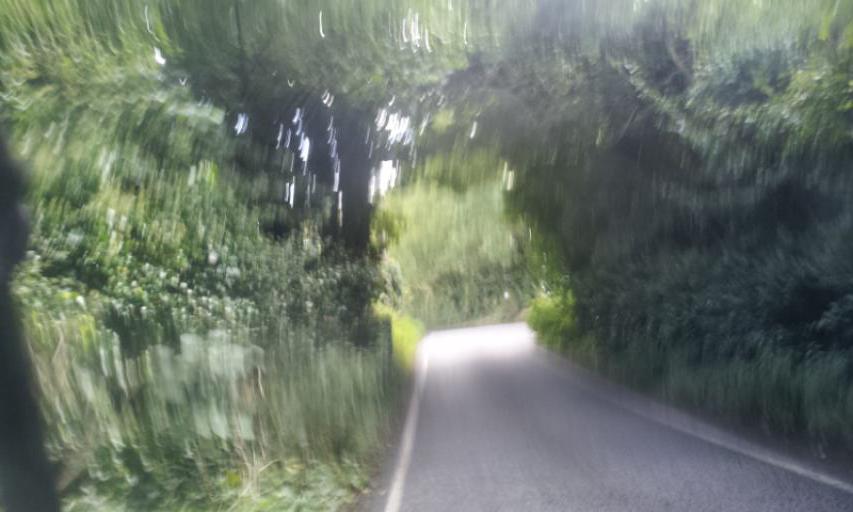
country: GB
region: England
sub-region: Kent
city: Rainham
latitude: 51.3670
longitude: 0.6329
